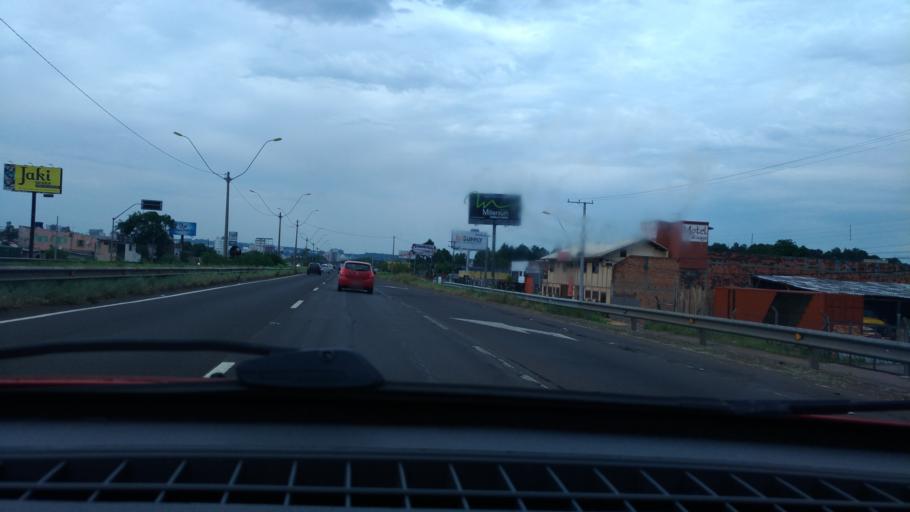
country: BR
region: Rio Grande do Sul
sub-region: Sao Leopoldo
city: Sao Leopoldo
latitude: -29.7512
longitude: -51.1516
